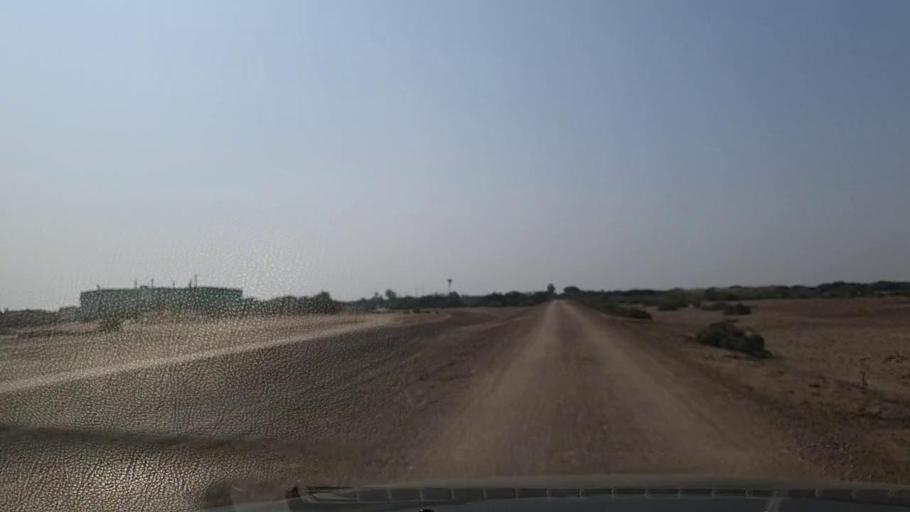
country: PK
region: Sindh
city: Mirpur Sakro
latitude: 24.4253
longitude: 67.7085
